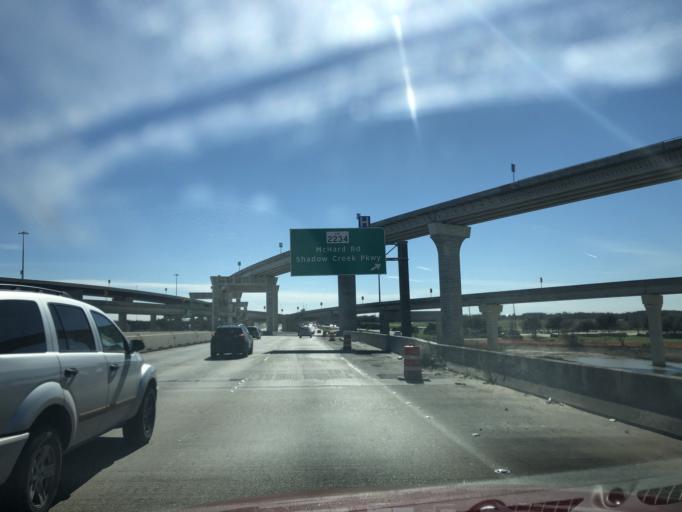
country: US
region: Texas
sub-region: Brazoria County
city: Brookside Village
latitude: 29.5964
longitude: -95.3872
